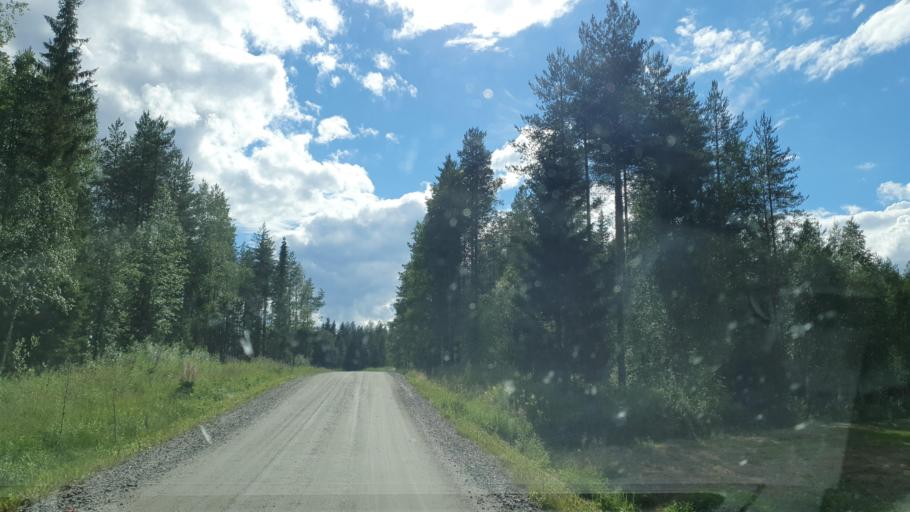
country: FI
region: Kainuu
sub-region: Kehys-Kainuu
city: Kuhmo
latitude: 64.1314
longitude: 29.6542
